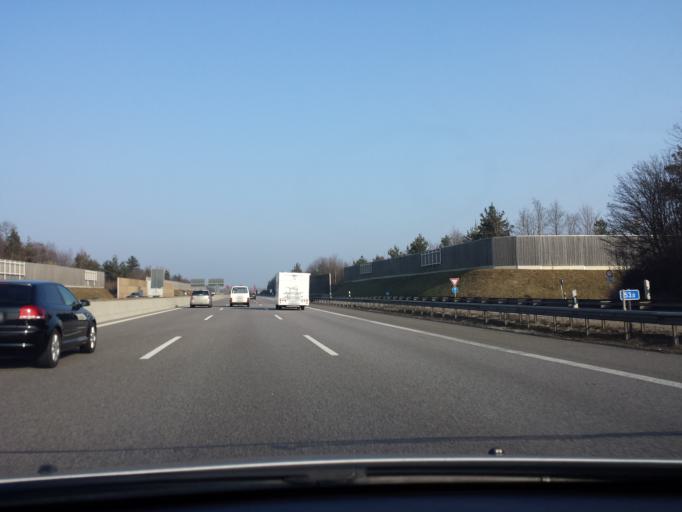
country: DE
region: Bavaria
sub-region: Swabia
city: Gersthofen
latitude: 48.4144
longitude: 10.8759
